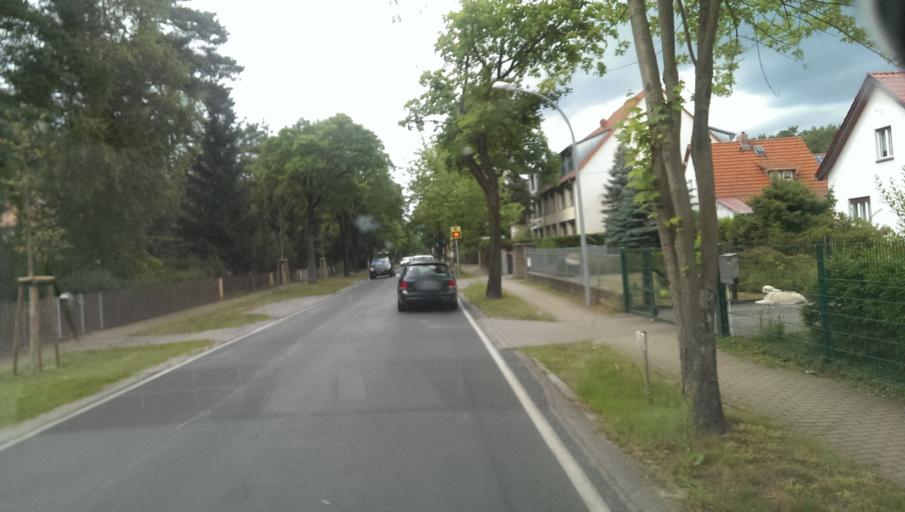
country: DE
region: Brandenburg
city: Fichtenwalde
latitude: 52.2795
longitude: 12.8906
